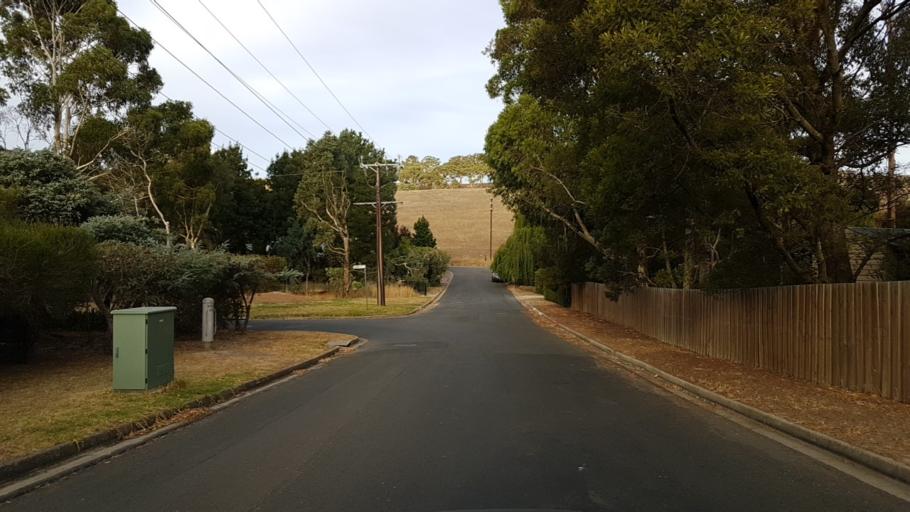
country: AU
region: South Australia
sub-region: Mount Barker
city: Nairne
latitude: -35.0289
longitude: 138.9099
